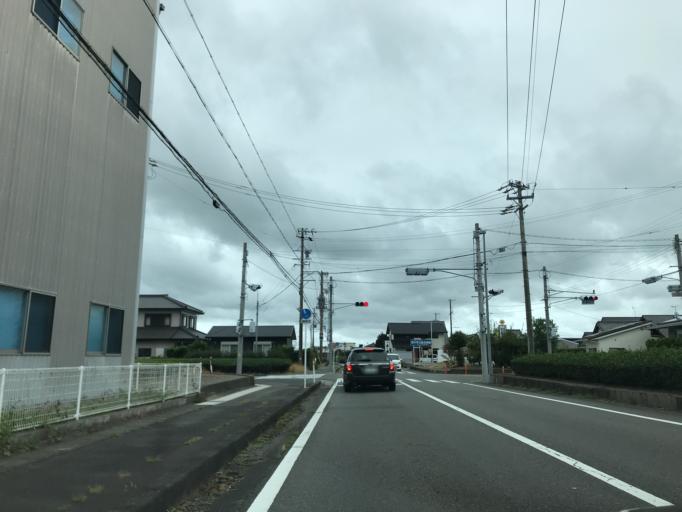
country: JP
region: Shizuoka
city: Kanaya
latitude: 34.7545
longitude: 138.1325
